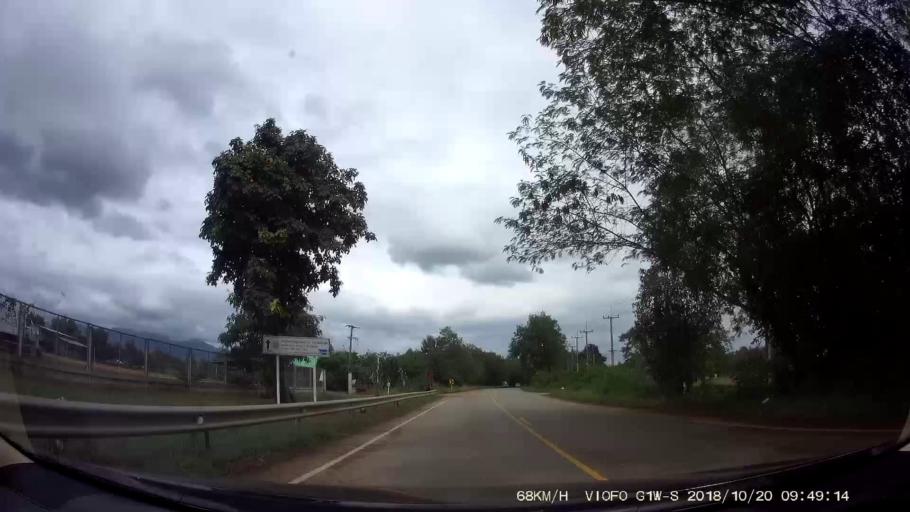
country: TH
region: Chaiyaphum
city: Khon San
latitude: 16.5173
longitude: 101.9062
